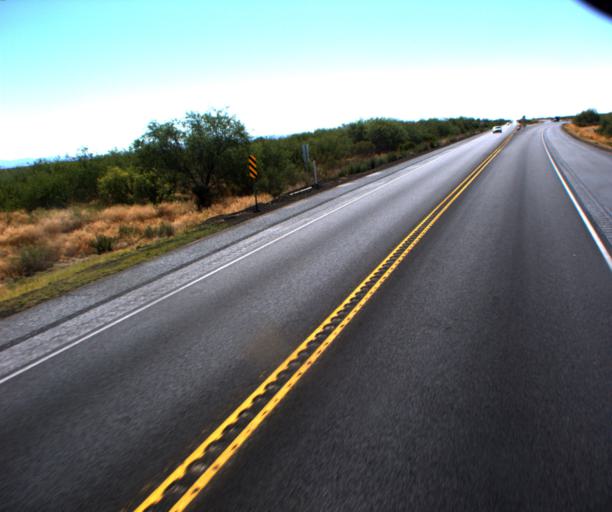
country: US
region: Arizona
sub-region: Yavapai County
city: Congress
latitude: 34.1028
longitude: -112.9210
